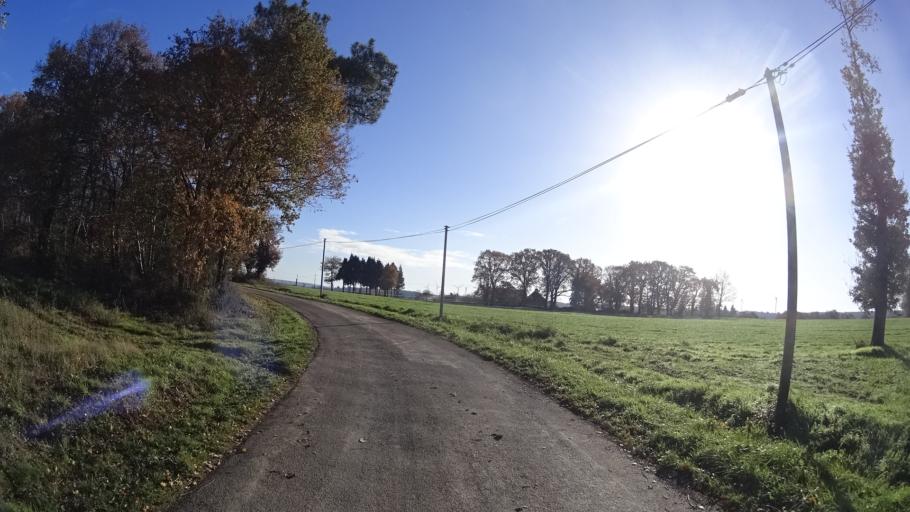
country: FR
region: Brittany
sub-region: Departement du Morbihan
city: Carentoir
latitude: 47.7944
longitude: -2.1997
